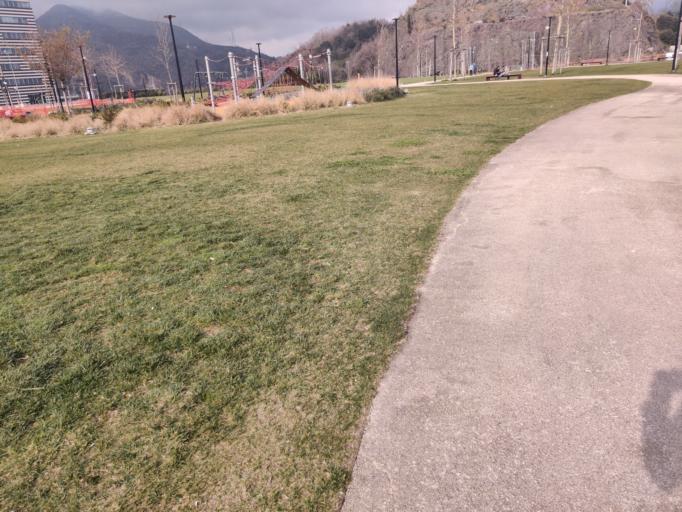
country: IT
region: Liguria
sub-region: Provincia di Genova
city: San Teodoro
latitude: 44.4240
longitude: 8.8634
